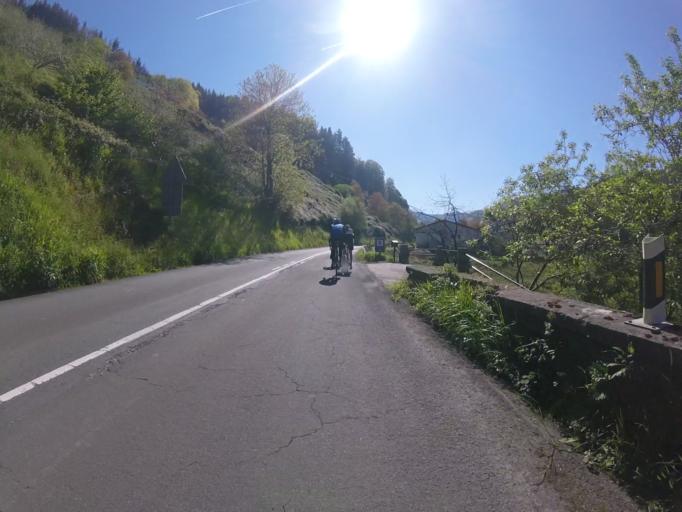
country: ES
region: Basque Country
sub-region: Provincia de Guipuzcoa
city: Errezil
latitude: 43.1708
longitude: -2.1970
